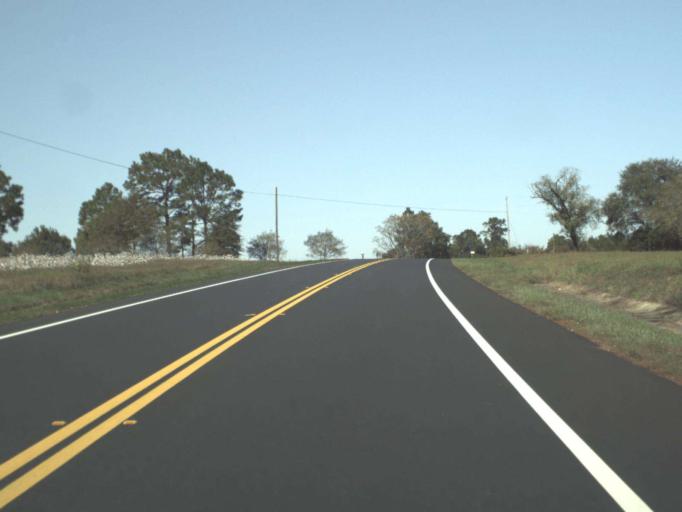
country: US
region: Florida
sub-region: Walton County
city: DeFuniak Springs
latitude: 30.8269
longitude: -86.2291
